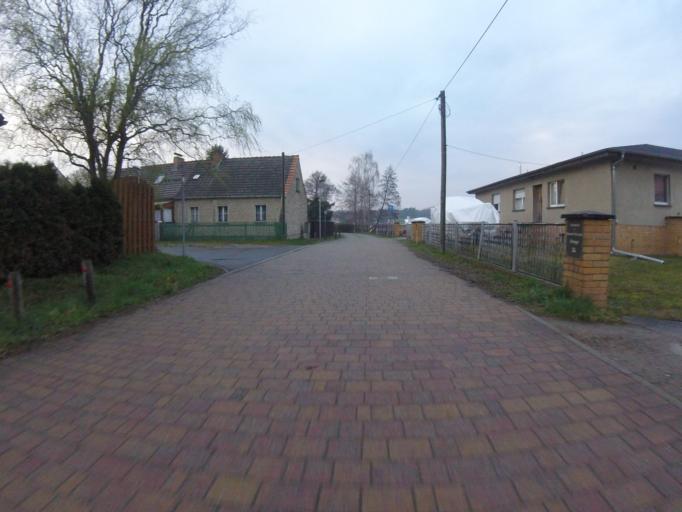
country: DE
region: Brandenburg
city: Konigs Wusterhausen
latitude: 52.2933
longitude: 13.6733
